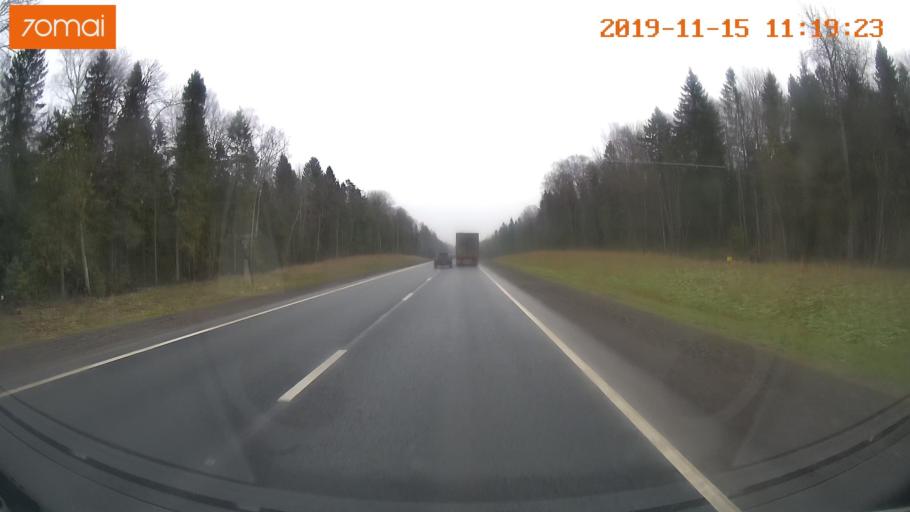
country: RU
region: Vologda
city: Molochnoye
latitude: 59.1382
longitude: 39.2903
